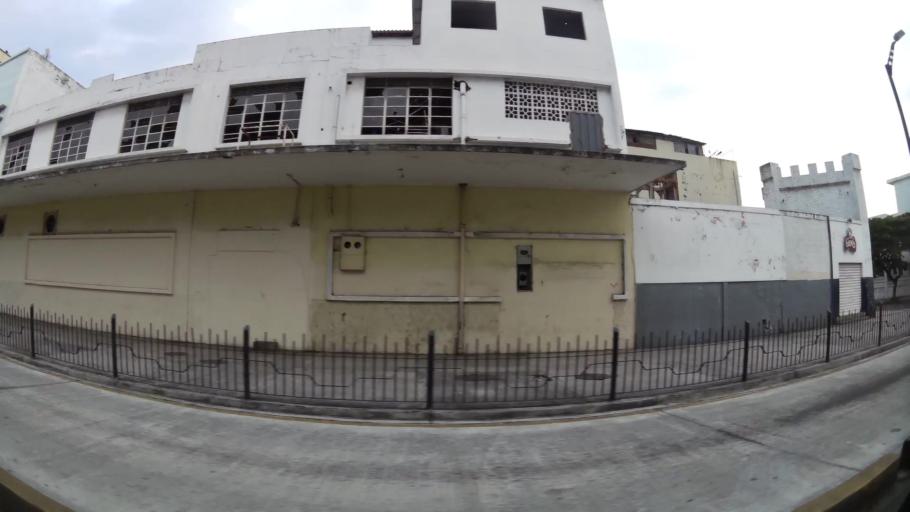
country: EC
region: Guayas
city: Guayaquil
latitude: -2.2070
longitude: -79.8853
